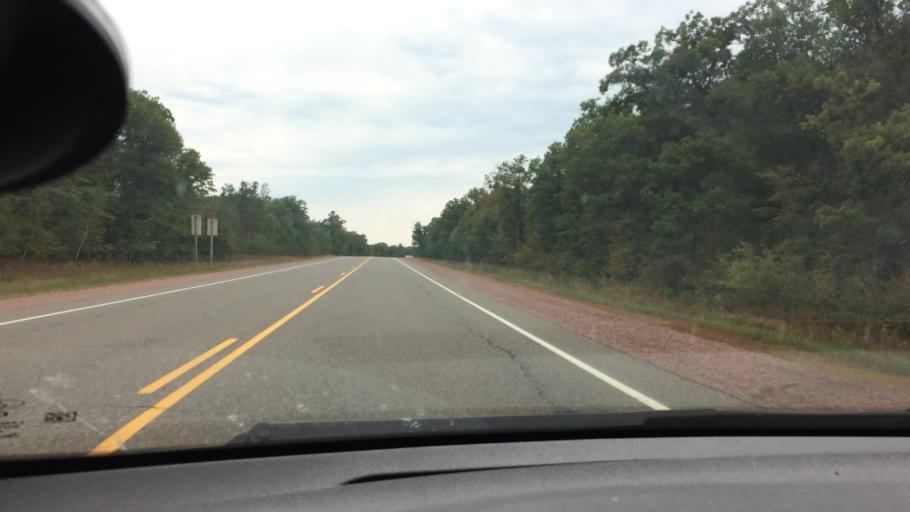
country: US
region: Wisconsin
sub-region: Clark County
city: Neillsville
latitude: 44.5663
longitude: -90.7141
